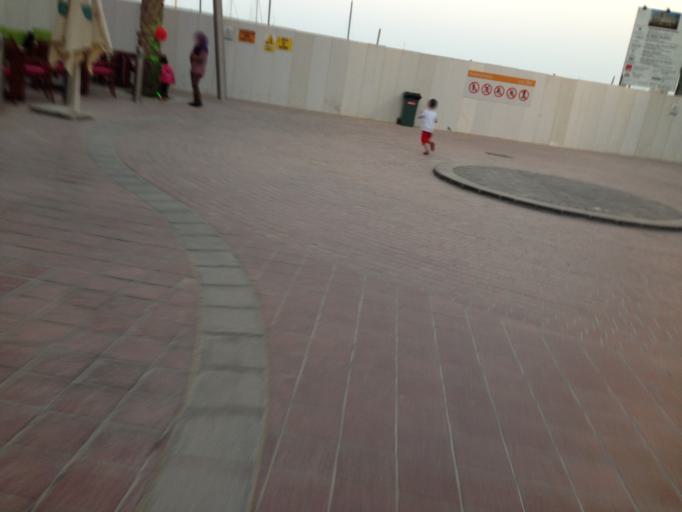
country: OM
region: Muhafazat Masqat
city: As Sib al Jadidah
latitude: 23.6299
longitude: 58.2668
